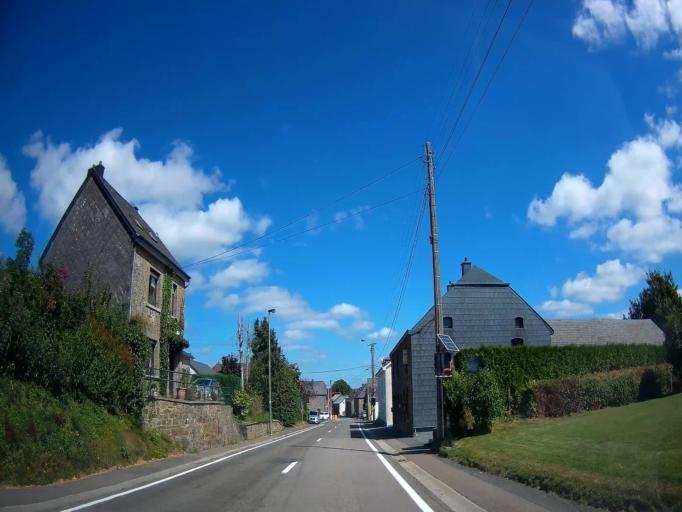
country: BE
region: Wallonia
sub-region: Province du Luxembourg
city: Bertogne
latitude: 50.0817
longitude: 5.6656
